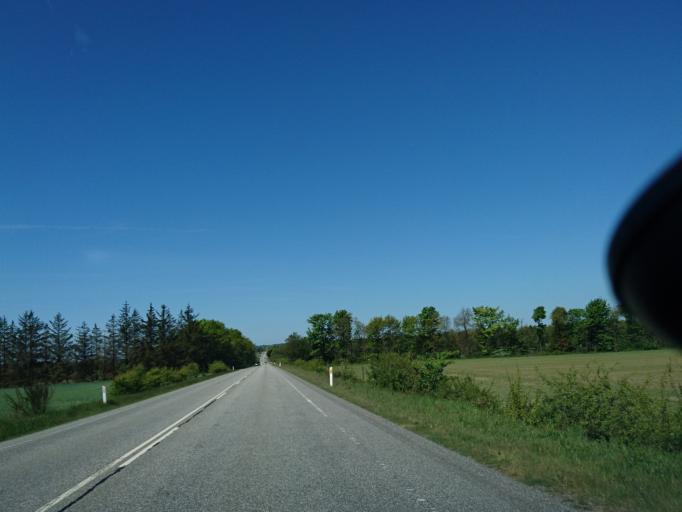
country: DK
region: North Denmark
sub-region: Hjorring Kommune
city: Sindal
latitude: 57.4655
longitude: 10.2733
